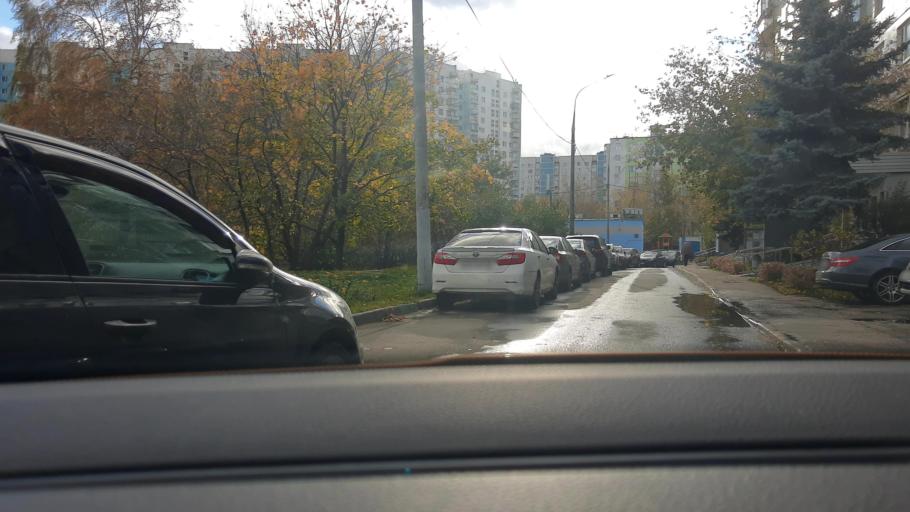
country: RU
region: Moscow
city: Strogino
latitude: 55.8083
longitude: 37.4119
